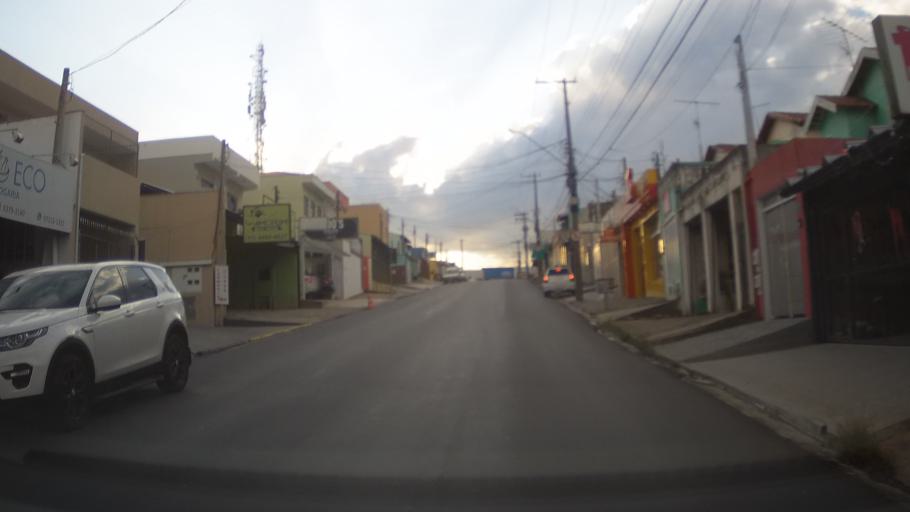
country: BR
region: Sao Paulo
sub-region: Jundiai
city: Jundiai
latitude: -23.1871
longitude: -46.9642
